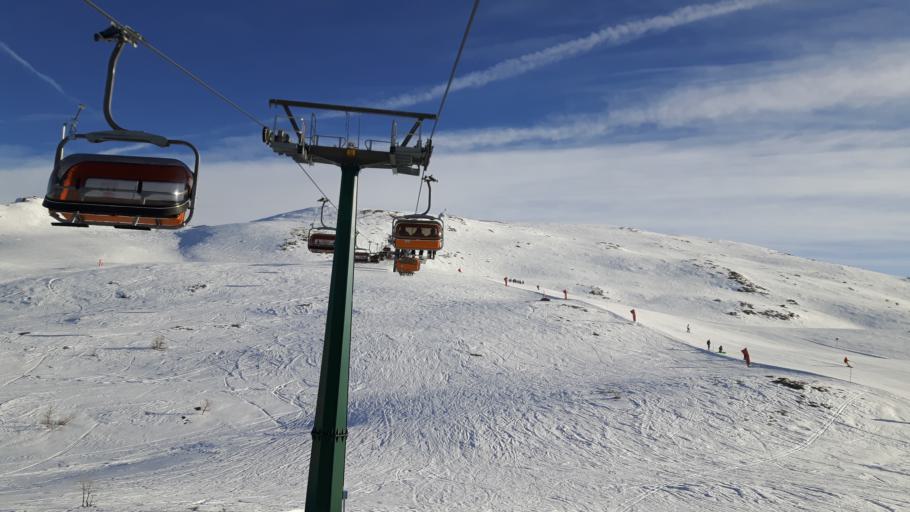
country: IT
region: Trentino-Alto Adige
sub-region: Provincia di Trento
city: Moena
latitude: 46.3433
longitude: 11.7188
